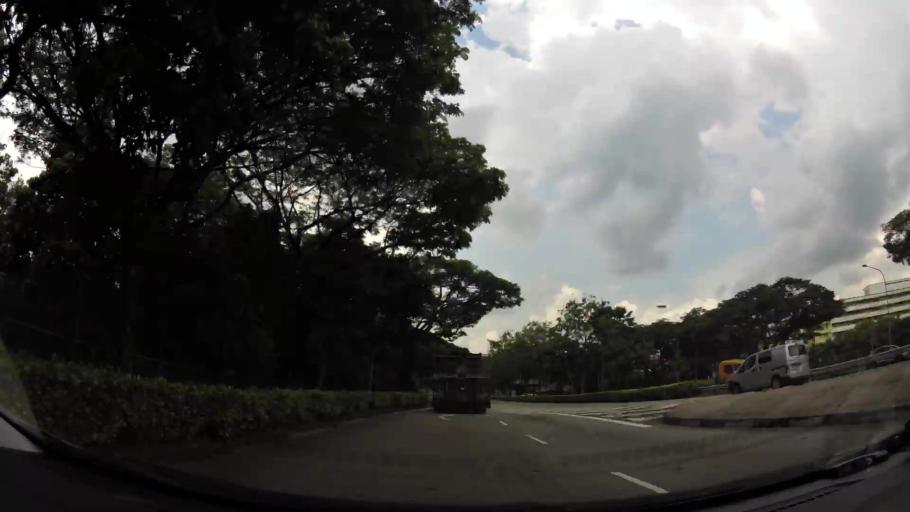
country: SG
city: Singapore
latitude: 1.2741
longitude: 103.8300
